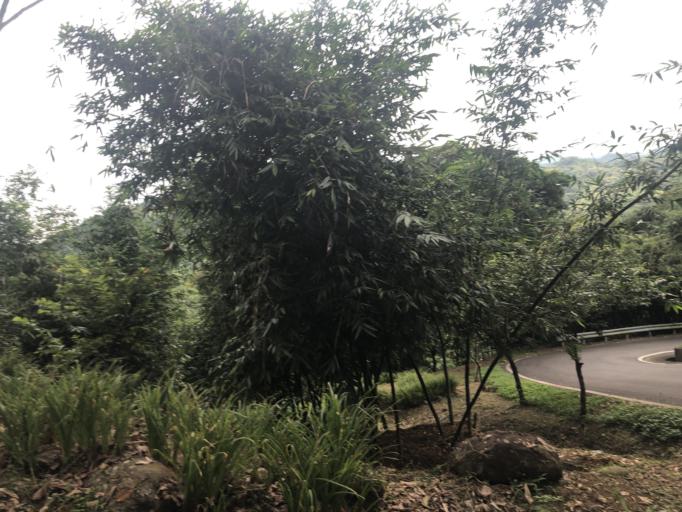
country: TW
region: Taiwan
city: Daxi
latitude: 24.8842
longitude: 121.4182
